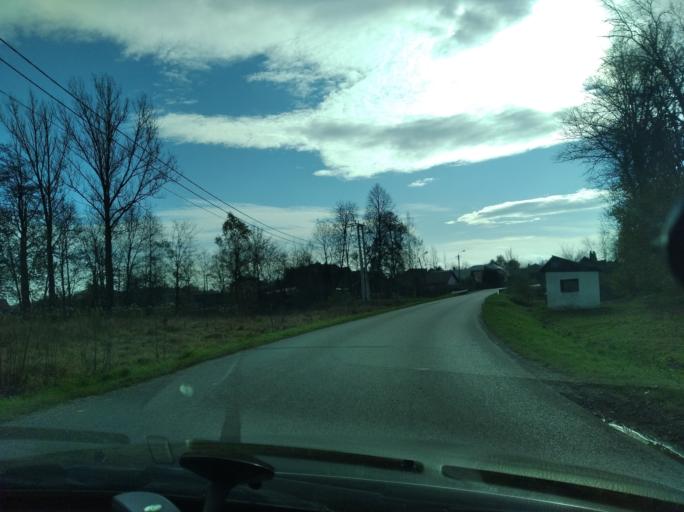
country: PL
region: Subcarpathian Voivodeship
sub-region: Powiat ropczycko-sedziszowski
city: Ostrow
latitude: 50.0962
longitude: 21.5543
